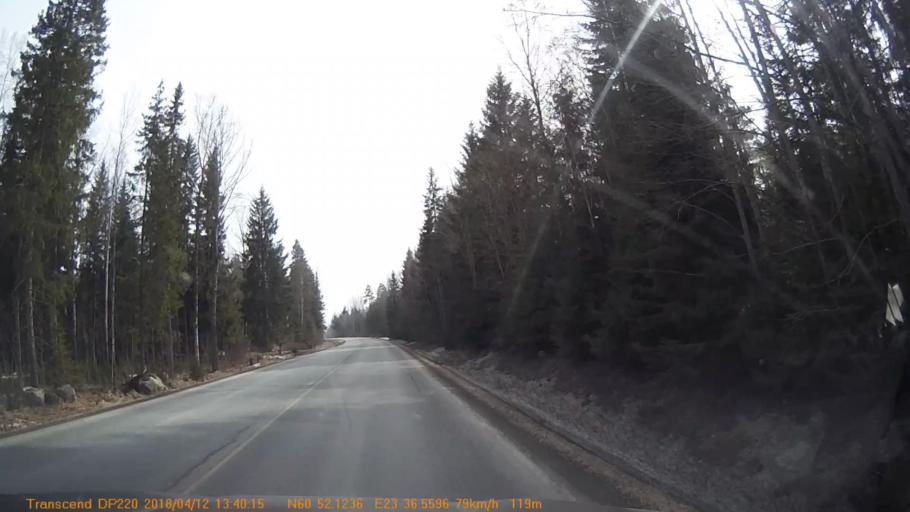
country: FI
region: Haeme
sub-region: Forssa
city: Forssa
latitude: 60.8680
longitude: 23.6098
